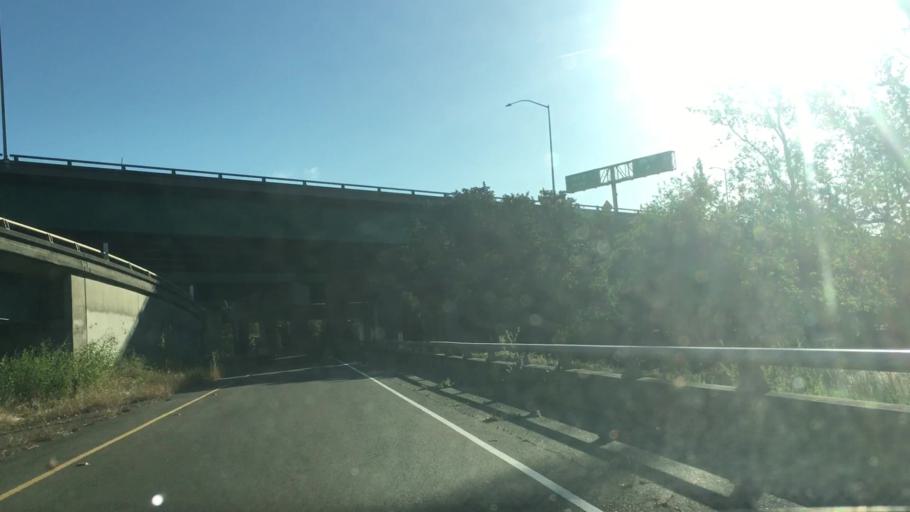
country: US
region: California
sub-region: Sacramento County
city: Sacramento
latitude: 38.5677
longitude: -121.5109
